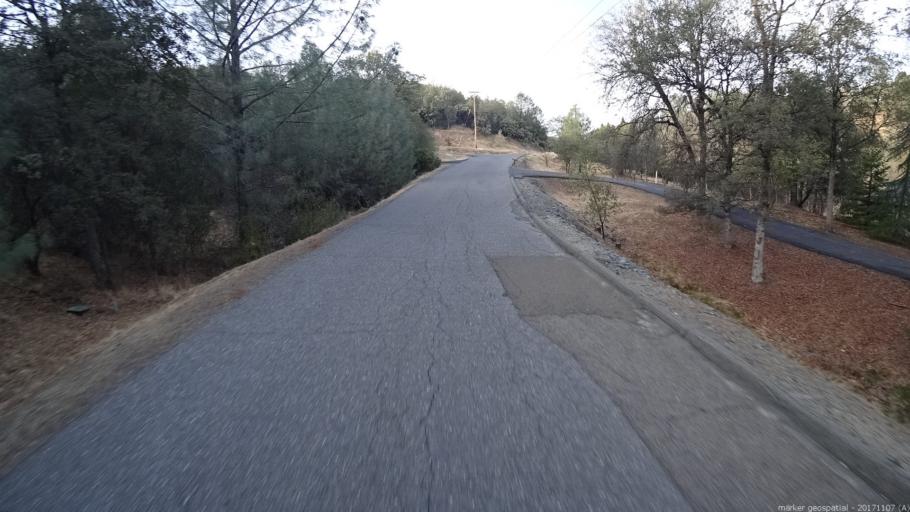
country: US
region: California
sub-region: Shasta County
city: Shasta
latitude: 40.5305
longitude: -122.4866
